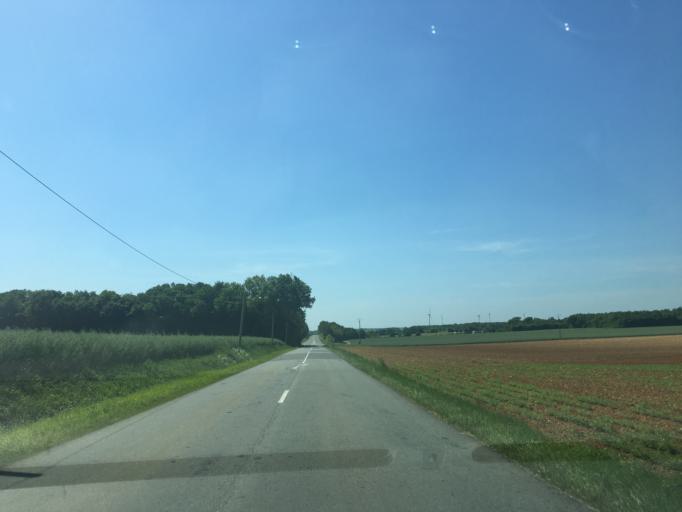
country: FR
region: Poitou-Charentes
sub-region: Departement des Deux-Sevres
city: Beauvoir-sur-Niort
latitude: 46.0774
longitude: -0.5237
